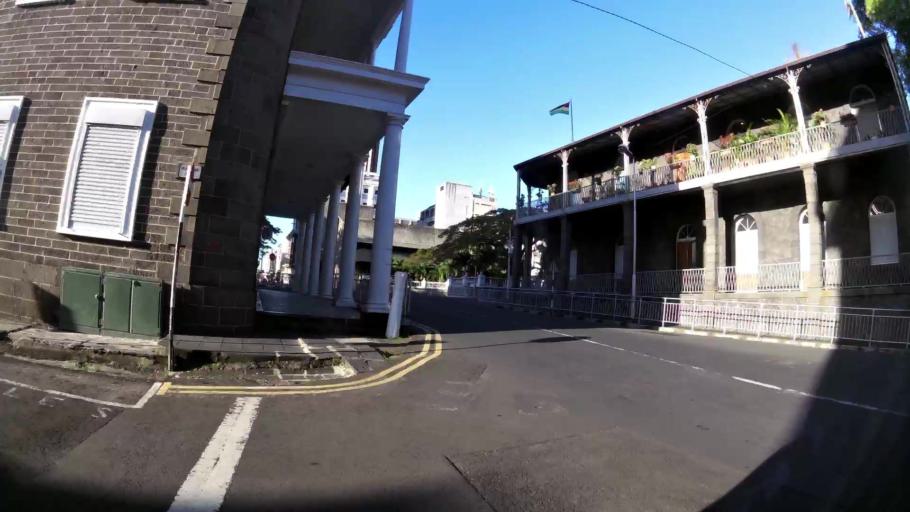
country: MU
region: Port Louis
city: Port Louis
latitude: -20.1628
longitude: 57.5023
